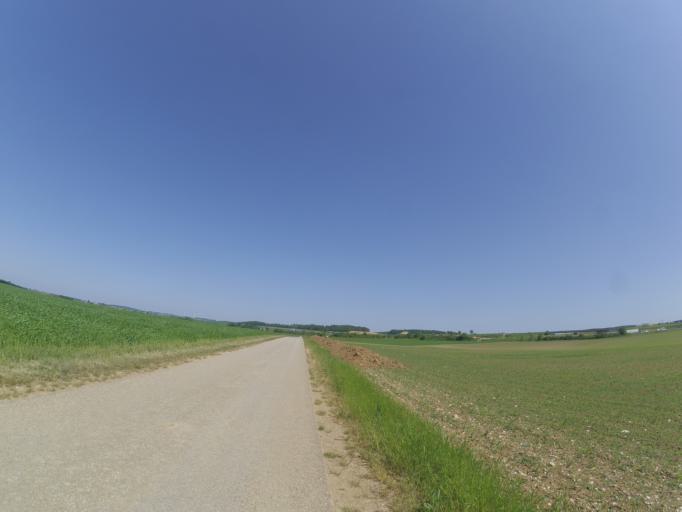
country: DE
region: Baden-Wuerttemberg
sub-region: Tuebingen Region
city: Merklingen
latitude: 48.5217
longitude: 9.7569
